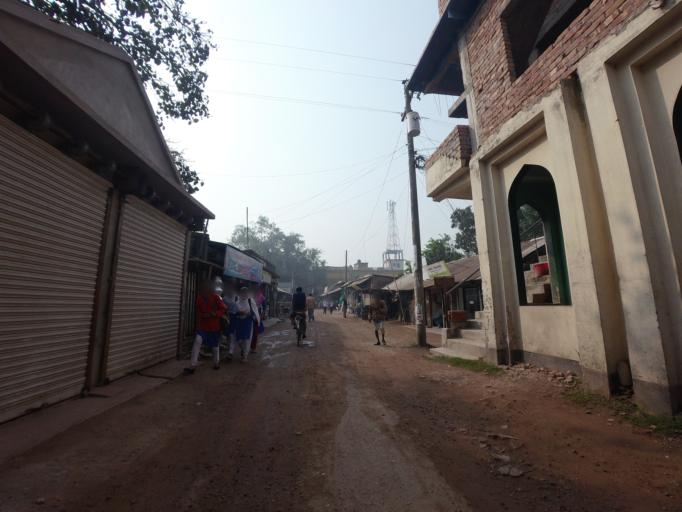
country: BD
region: Khulna
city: Narail
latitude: 23.1099
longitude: 89.4965
